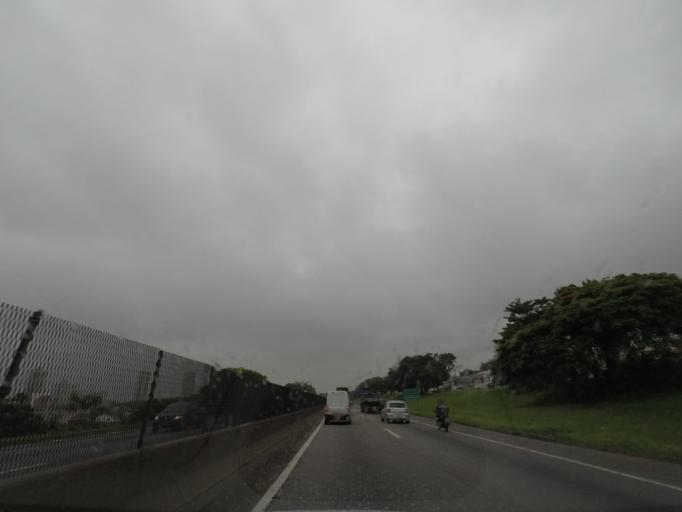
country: BR
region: Sao Paulo
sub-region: Taubate
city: Taubate
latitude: -23.0420
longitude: -45.5727
